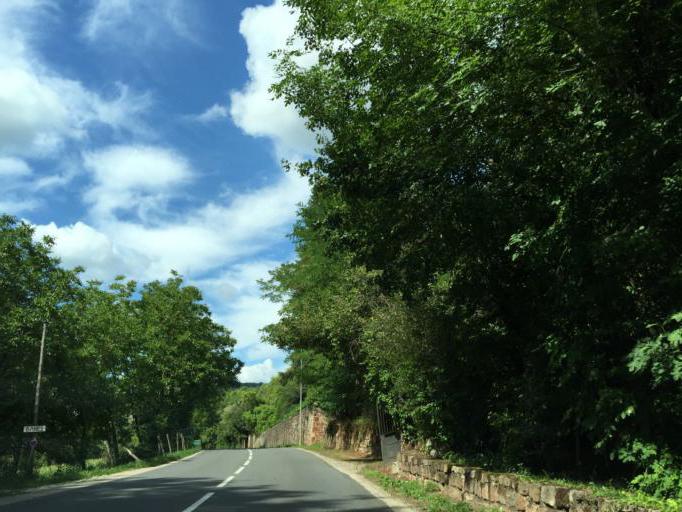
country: FR
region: Midi-Pyrenees
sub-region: Departement de l'Aveyron
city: Marcillac-Vallon
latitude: 44.4647
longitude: 2.4691
